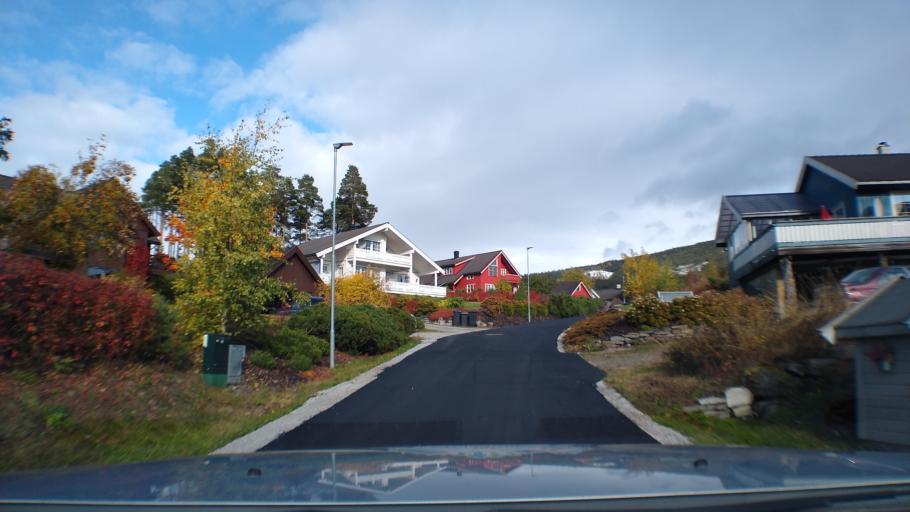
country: NO
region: Oppland
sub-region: Ringebu
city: Ringebu
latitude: 61.5328
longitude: 10.1315
